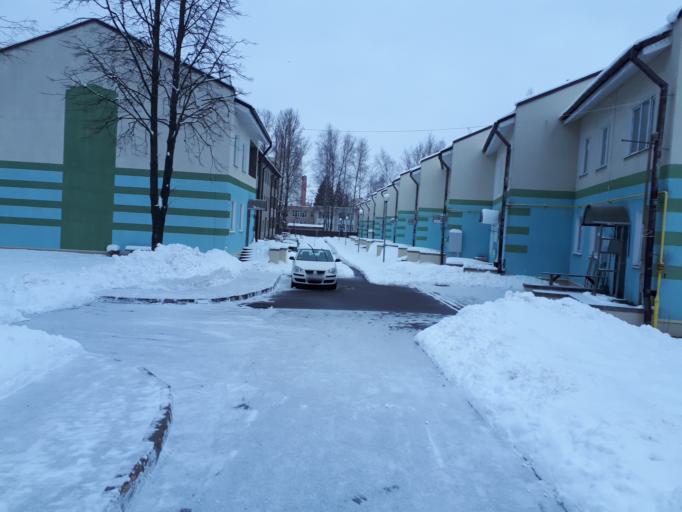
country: BY
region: Vitebsk
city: Vitebsk
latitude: 55.1747
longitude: 30.2195
